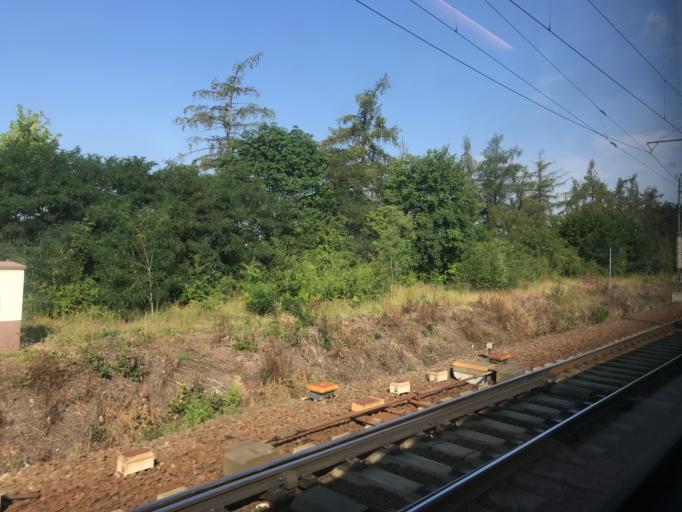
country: CZ
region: Jihocesky
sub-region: Okres Tabor
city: Tabor
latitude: 49.4174
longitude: 14.6732
